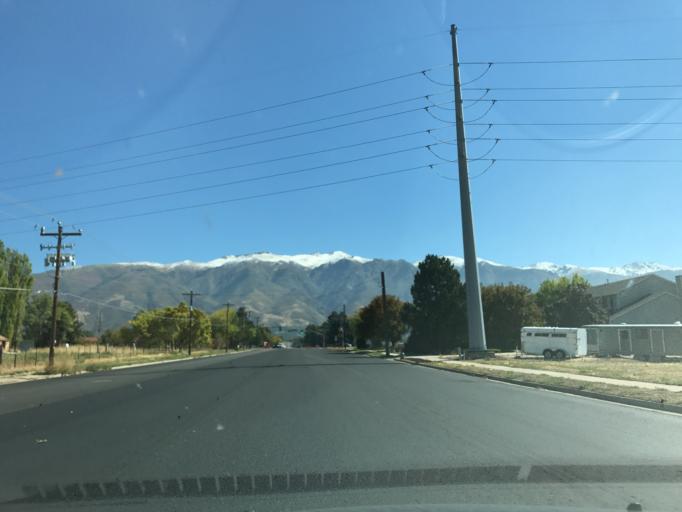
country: US
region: Utah
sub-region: Davis County
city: Hill Air Force Bace
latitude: 41.0889
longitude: -111.9526
